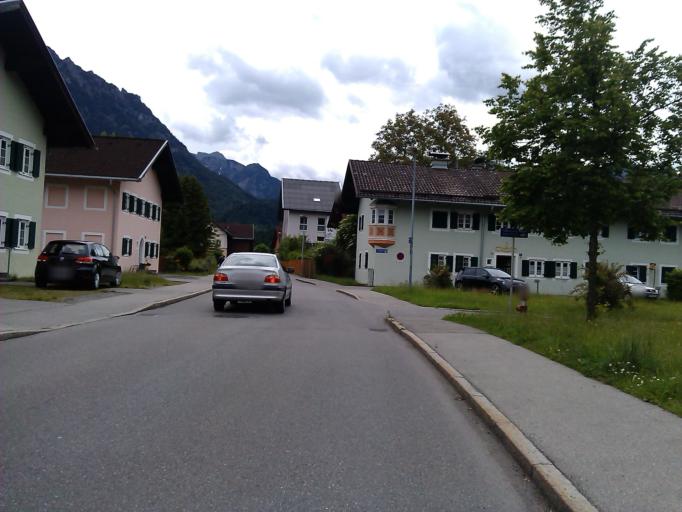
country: AT
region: Tyrol
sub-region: Politischer Bezirk Reutte
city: Reutte
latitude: 47.4854
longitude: 10.7185
